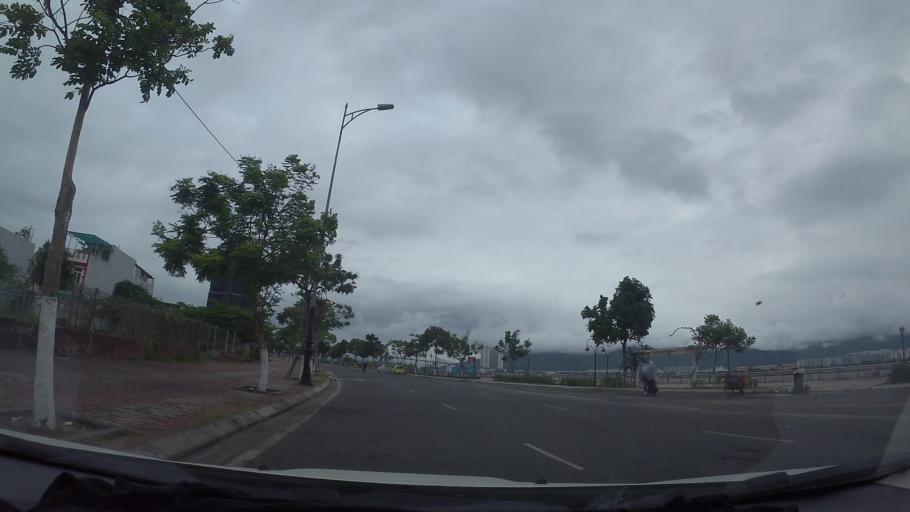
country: VN
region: Da Nang
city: Da Nang
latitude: 16.0831
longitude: 108.2233
